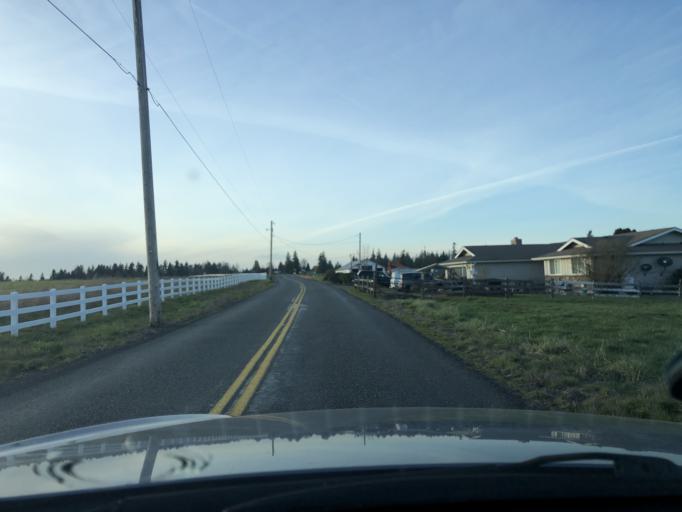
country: US
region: Washington
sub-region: Pierce County
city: Prairie Ridge
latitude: 47.1981
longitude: -122.1154
